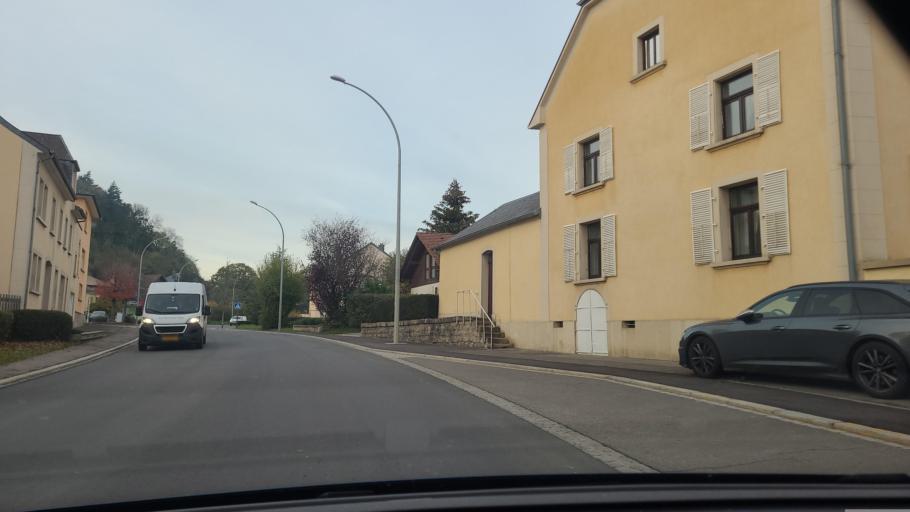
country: LU
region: Luxembourg
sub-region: Canton de Capellen
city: Garnich
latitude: 49.6170
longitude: 5.9520
